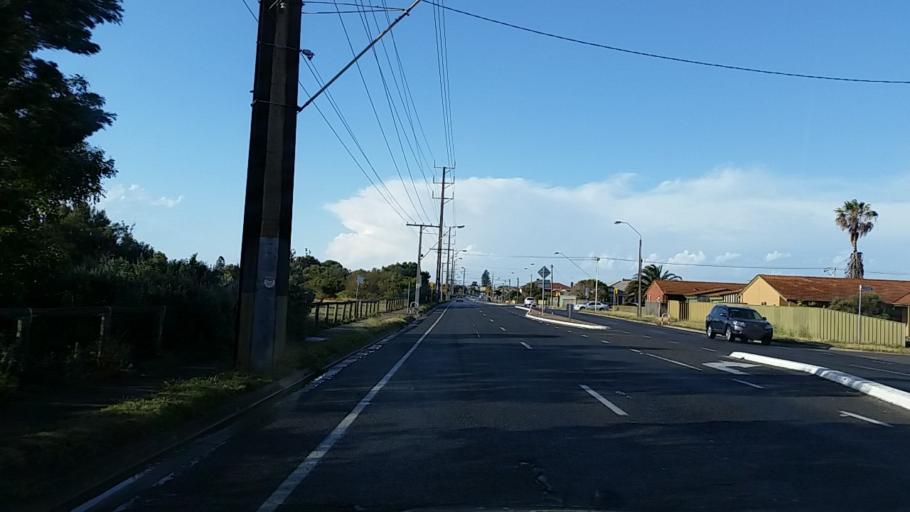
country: AU
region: South Australia
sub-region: Charles Sturt
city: West Lakes Shore
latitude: -34.8559
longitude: 138.4785
